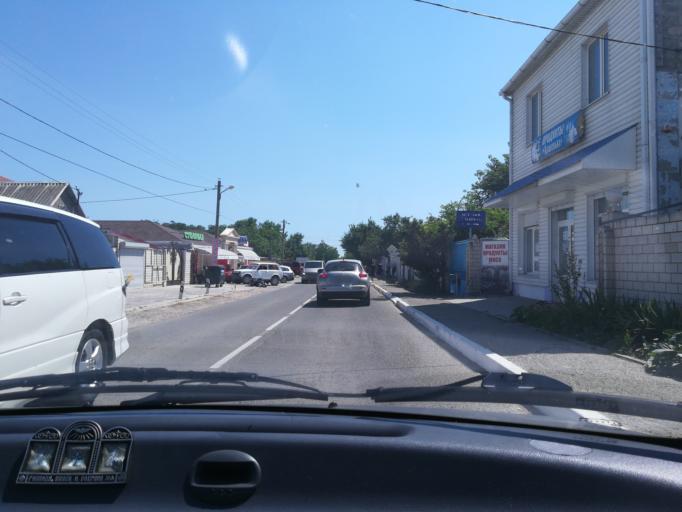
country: RU
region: Krasnodarskiy
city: Blagovetschenskaya
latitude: 45.0557
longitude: 37.1204
